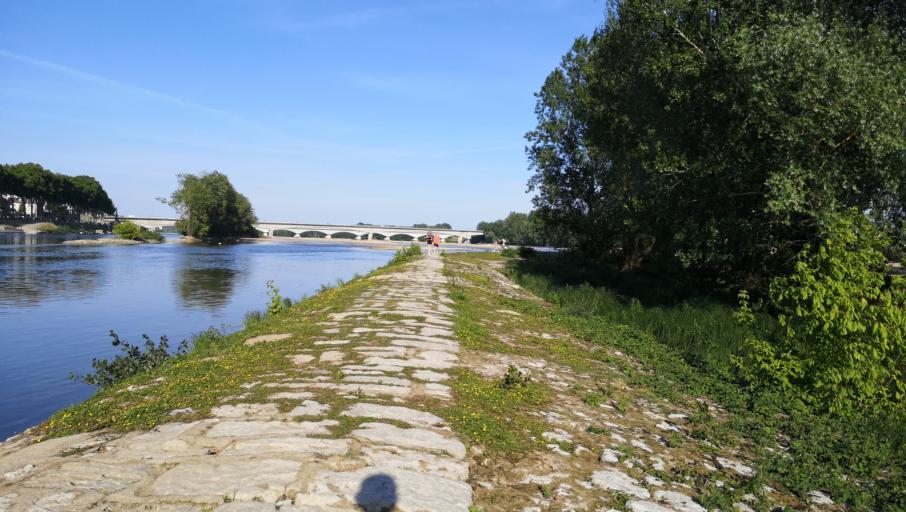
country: FR
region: Centre
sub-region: Departement du Loiret
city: Saint-Jean-le-Blanc
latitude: 47.8966
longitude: 1.9098
